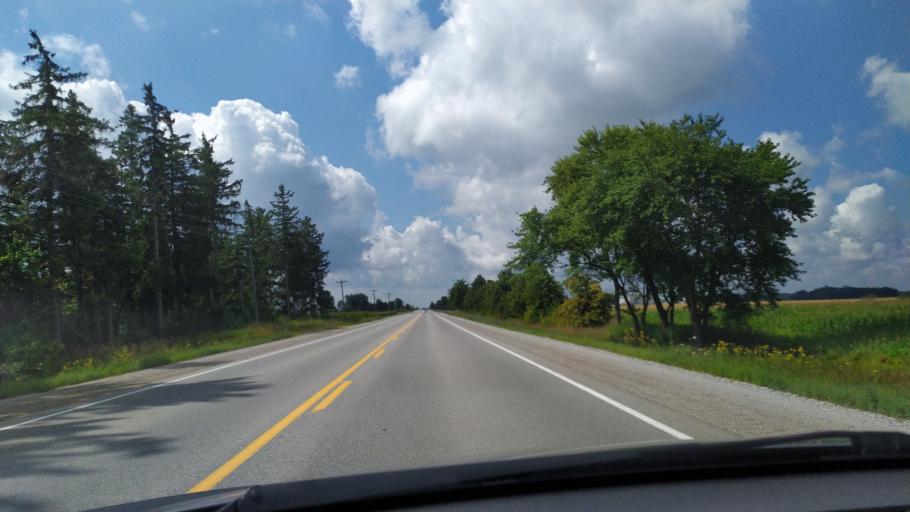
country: CA
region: Ontario
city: Huron East
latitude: 43.4178
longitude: -81.2407
